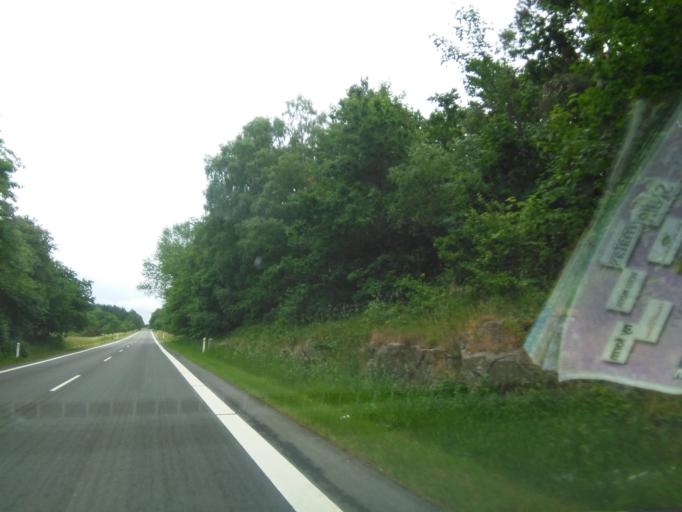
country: DK
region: Capital Region
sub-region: Bornholm Kommune
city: Akirkeby
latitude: 55.1184
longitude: 14.8398
